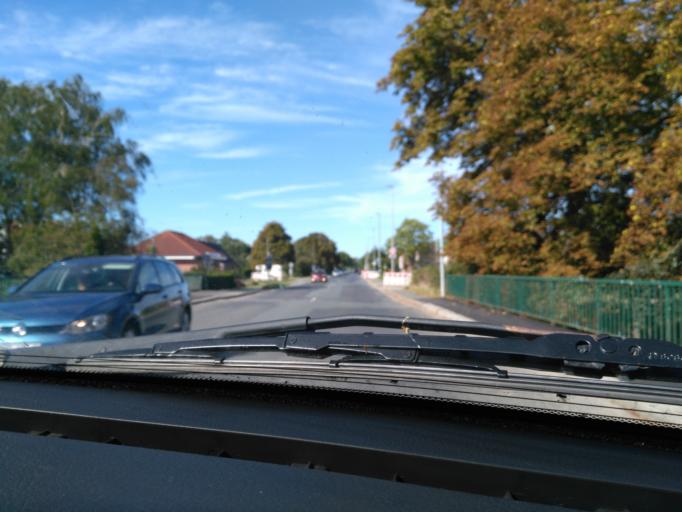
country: DE
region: Lower Saxony
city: Emden
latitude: 53.3349
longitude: 7.2727
